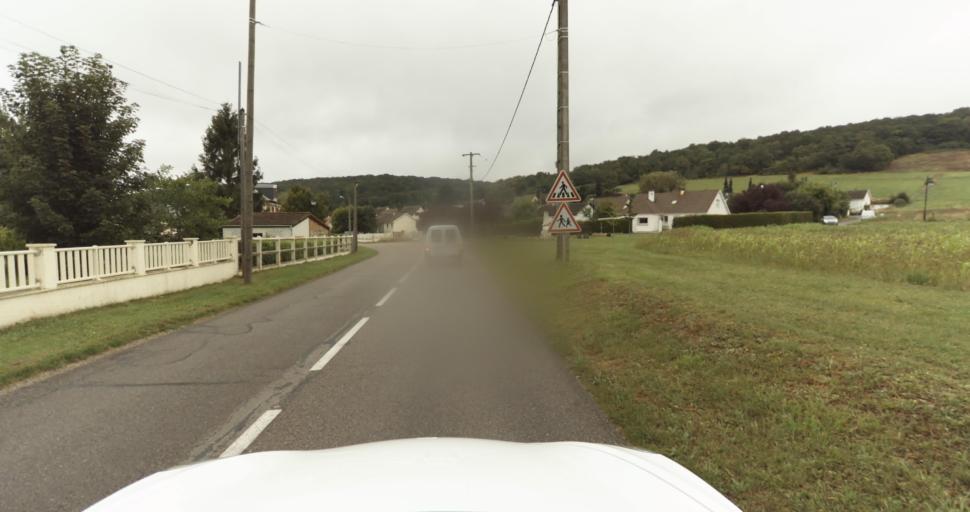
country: FR
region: Haute-Normandie
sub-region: Departement de l'Eure
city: Normanville
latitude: 49.0780
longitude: 1.1642
